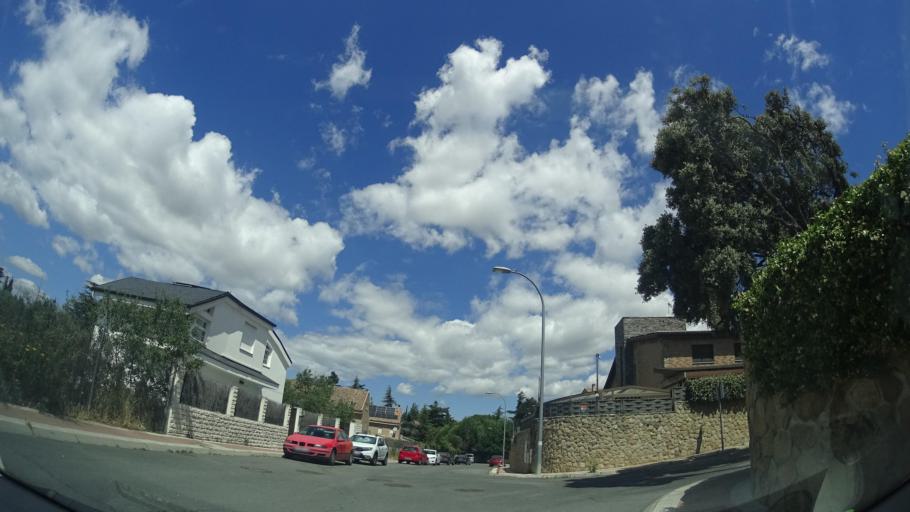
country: ES
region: Madrid
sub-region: Provincia de Madrid
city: Collado-Villalba
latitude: 40.6232
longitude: -3.9930
